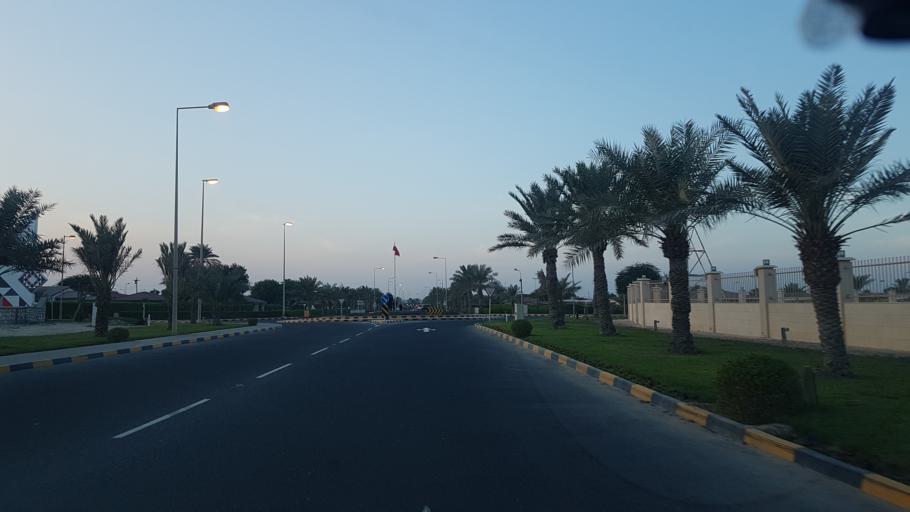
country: BH
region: Northern
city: Ar Rifa'
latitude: 26.0921
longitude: 50.5480
